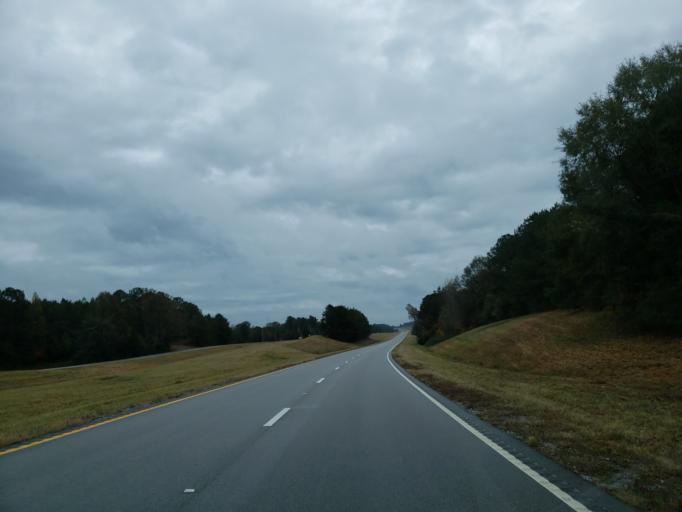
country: US
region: Mississippi
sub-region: Wayne County
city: Waynesboro
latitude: 31.6952
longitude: -88.7207
